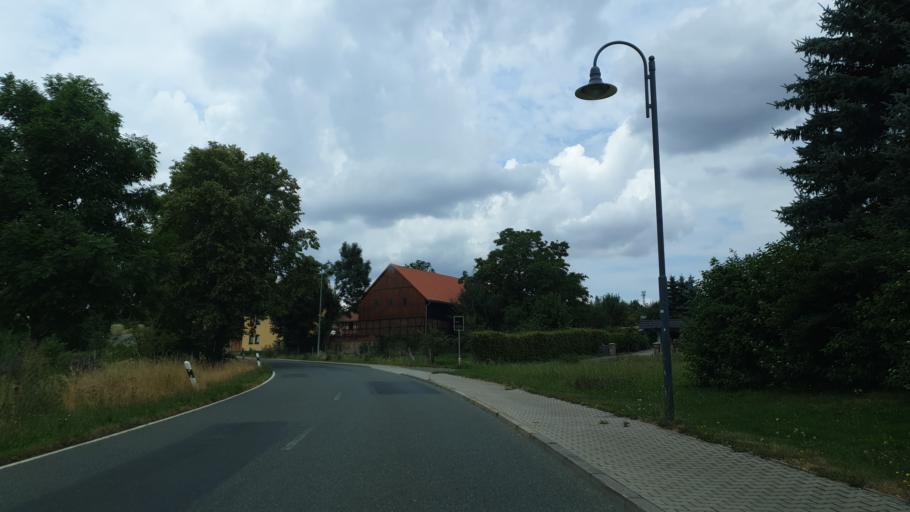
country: DE
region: Saxony
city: Hirschfeld
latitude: 50.6332
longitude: 12.4375
